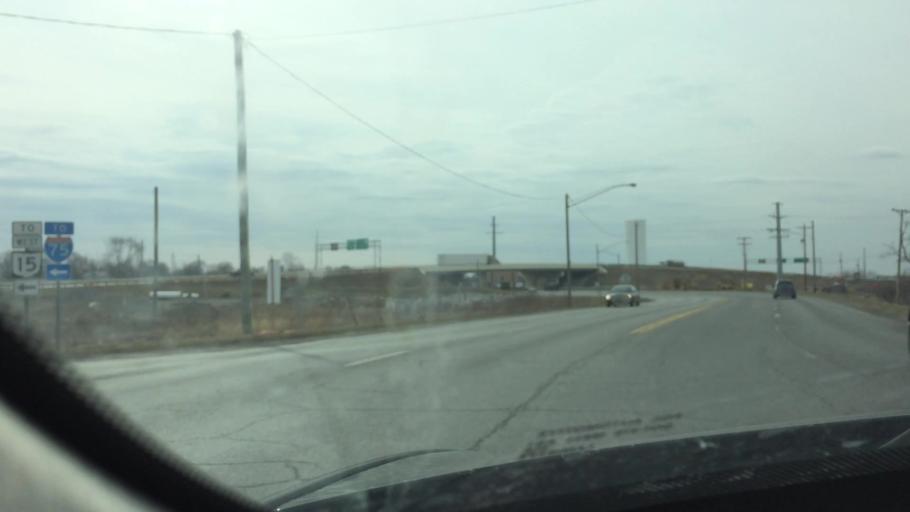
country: US
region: Ohio
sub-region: Hancock County
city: Findlay
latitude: 41.0244
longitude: -83.6656
